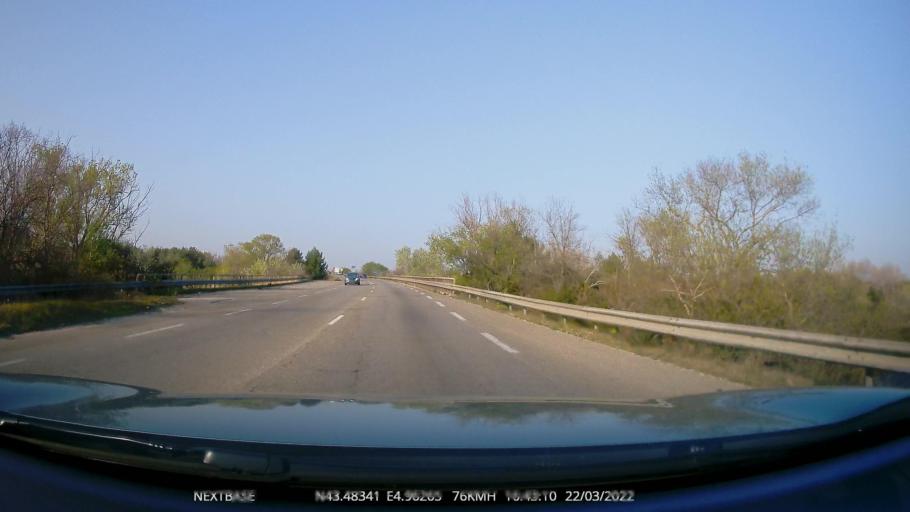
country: FR
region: Provence-Alpes-Cote d'Azur
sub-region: Departement des Bouches-du-Rhone
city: Istres
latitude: 43.4836
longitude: 4.9627
